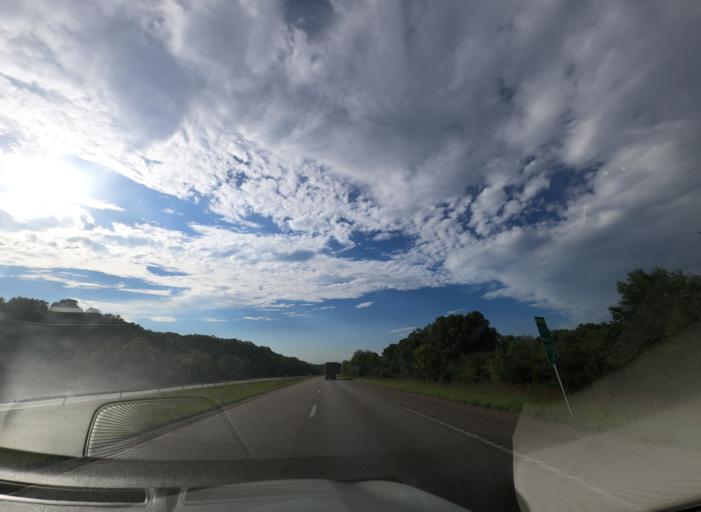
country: US
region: Missouri
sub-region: Sainte Genevieve County
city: Sainte Genevieve
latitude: 38.0346
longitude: -90.2552
